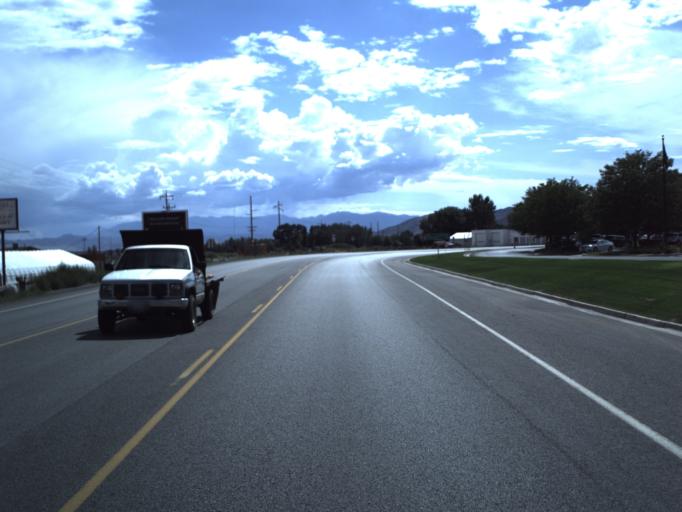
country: US
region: Utah
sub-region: Sevier County
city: Richfield
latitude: 38.7738
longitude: -112.0675
